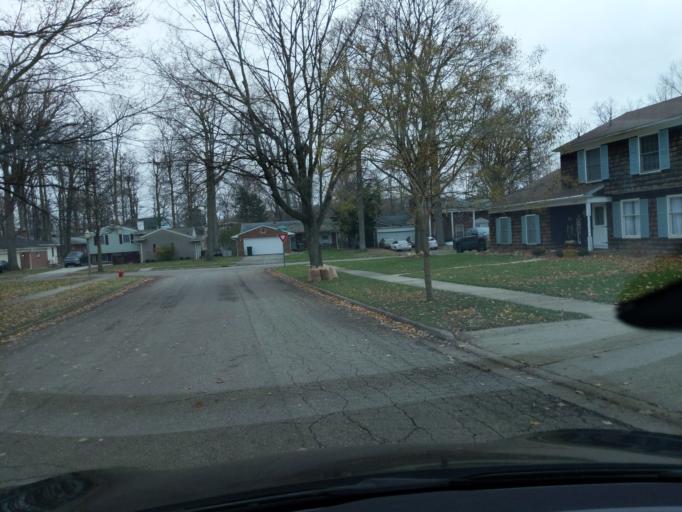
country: US
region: Michigan
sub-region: Ingham County
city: Edgemont Park
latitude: 42.7088
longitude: -84.5891
